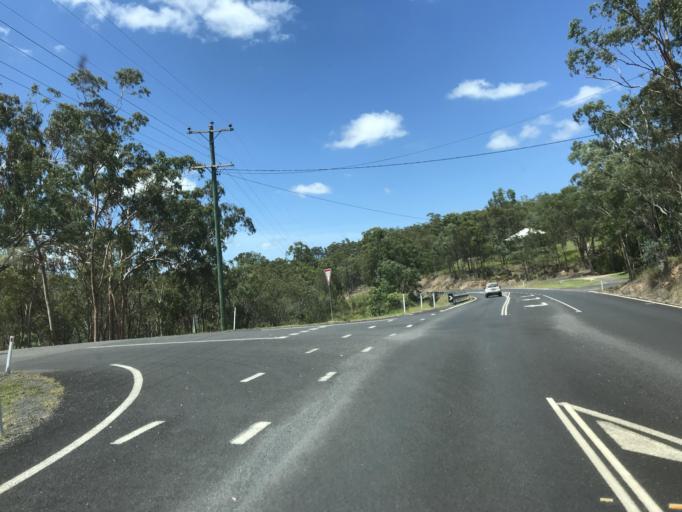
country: AU
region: Queensland
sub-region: Tablelands
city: Atherton
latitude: -17.3963
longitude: 145.3883
